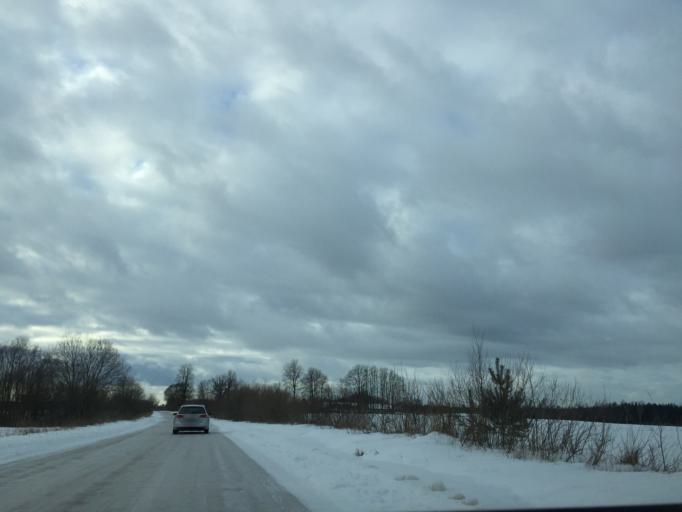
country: LV
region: Lielvarde
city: Lielvarde
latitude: 56.6163
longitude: 24.7705
